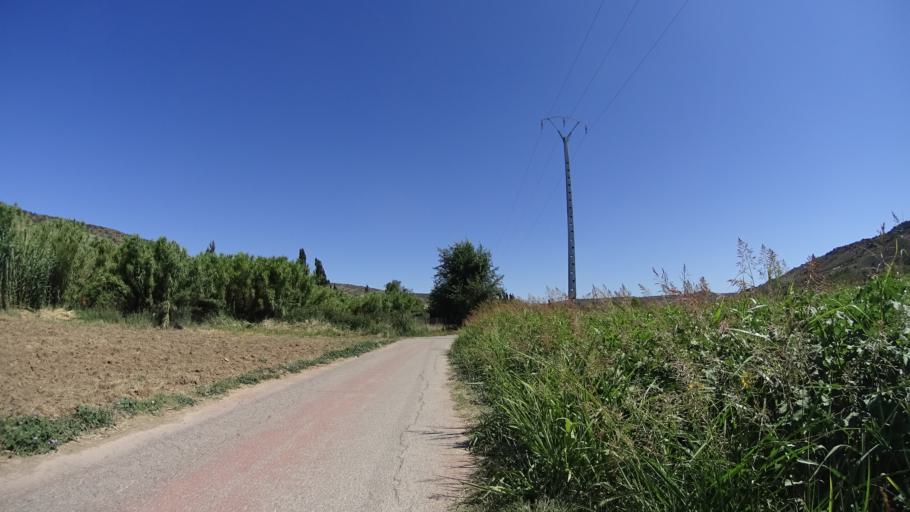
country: ES
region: Madrid
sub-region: Provincia de Madrid
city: Tielmes
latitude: 40.2351
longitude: -3.3214
